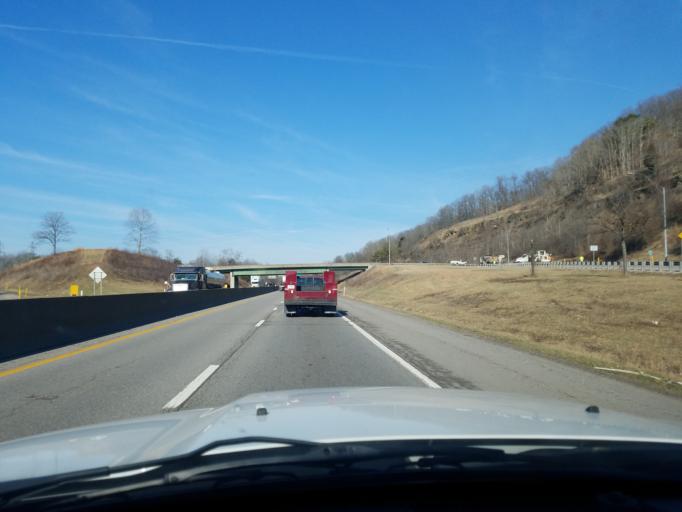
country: US
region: West Virginia
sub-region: Kanawha County
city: Nitro
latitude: 38.4474
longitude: -81.8474
